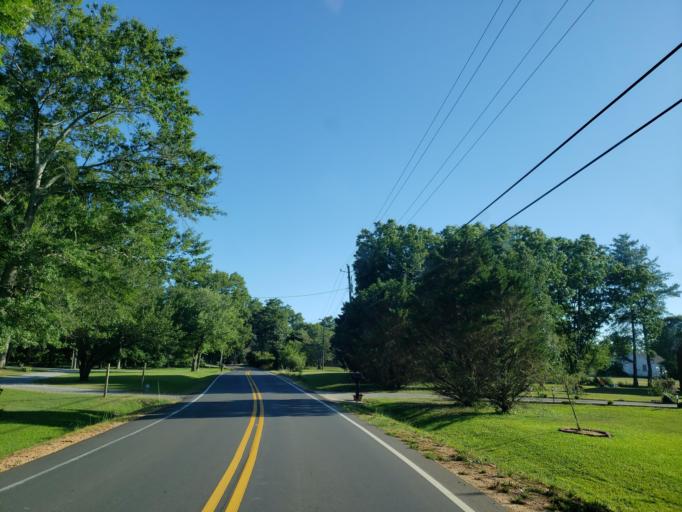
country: US
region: Georgia
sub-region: Floyd County
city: Shannon
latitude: 34.3574
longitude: -85.1439
